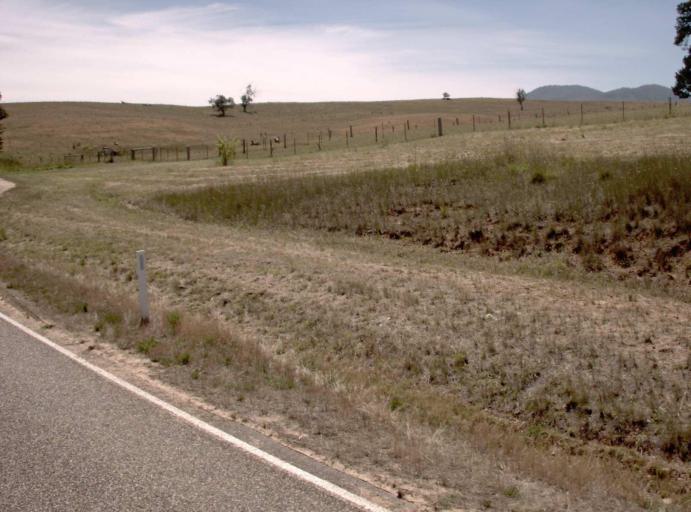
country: AU
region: Victoria
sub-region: Alpine
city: Mount Beauty
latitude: -37.0101
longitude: 147.6580
